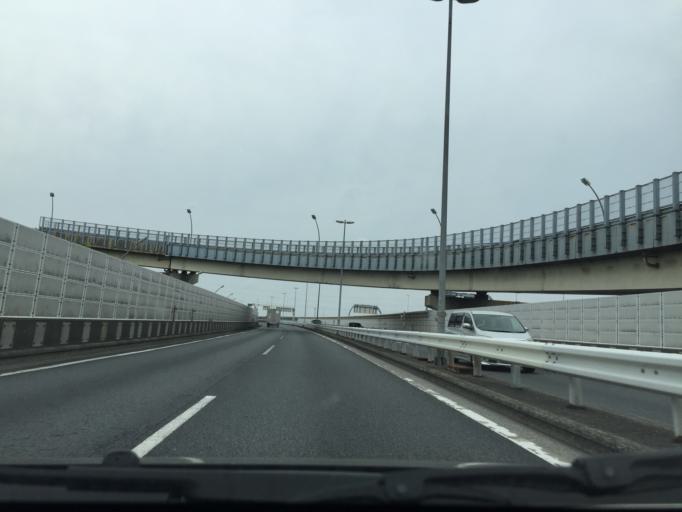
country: JP
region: Saitama
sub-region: Kawaguchi-shi
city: Hatogaya-honcho
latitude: 35.8529
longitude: 139.7340
